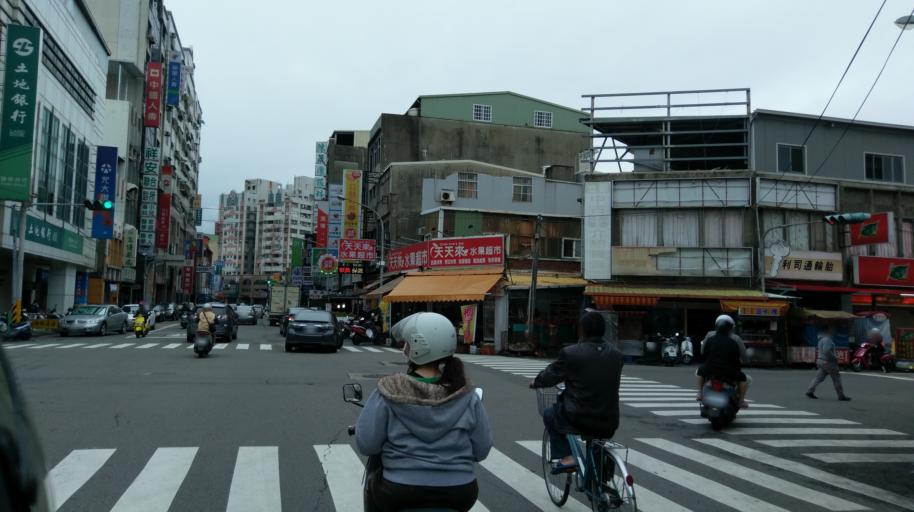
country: TW
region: Taiwan
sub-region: Hsinchu
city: Hsinchu
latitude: 24.6862
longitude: 120.9082
